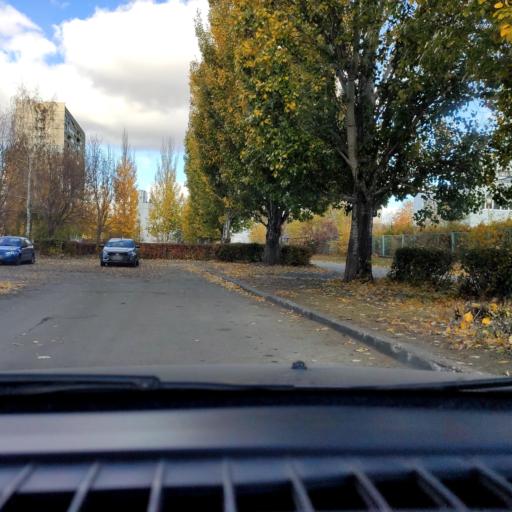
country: RU
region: Samara
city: Tol'yatti
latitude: 53.5038
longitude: 49.2804
